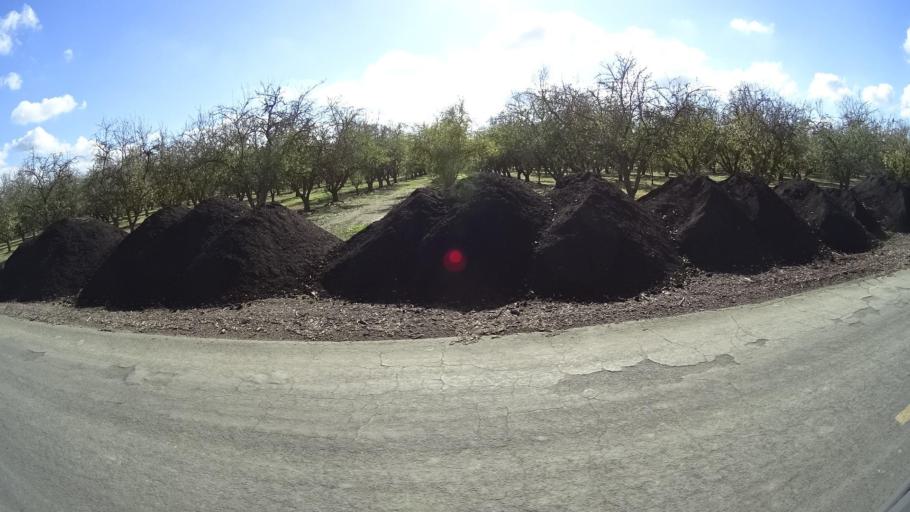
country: US
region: California
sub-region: Kern County
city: Delano
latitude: 35.7322
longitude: -119.3250
